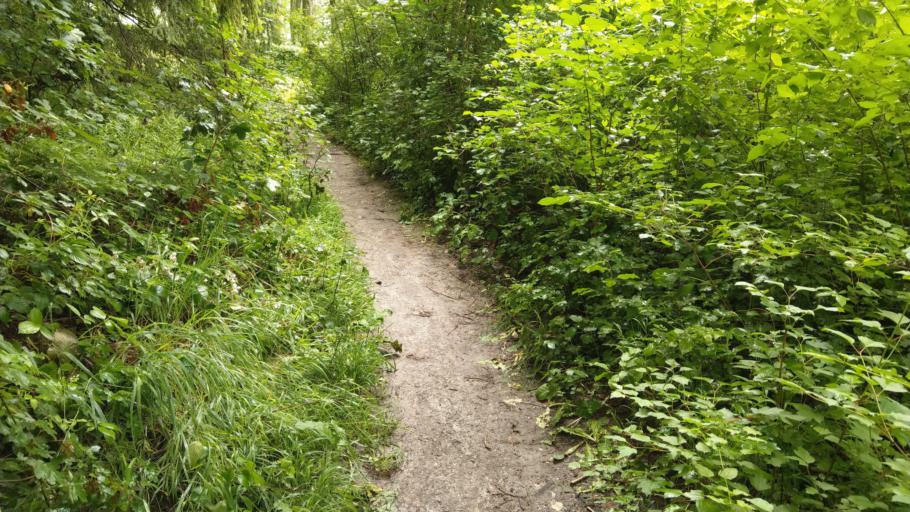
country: NL
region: Limburg
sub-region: Gemeente Vaals
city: Vaals
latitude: 50.7837
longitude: 6.0257
